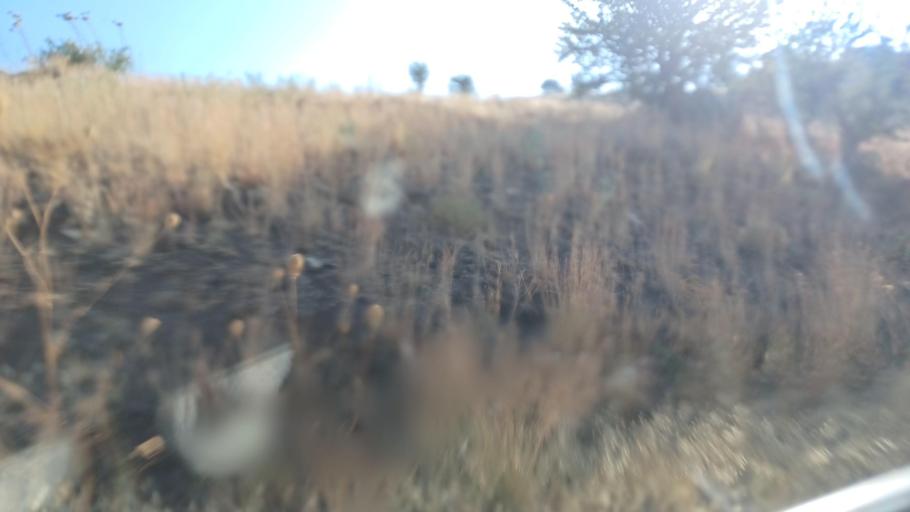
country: CY
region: Pafos
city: Mesogi
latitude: 34.8685
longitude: 32.6047
